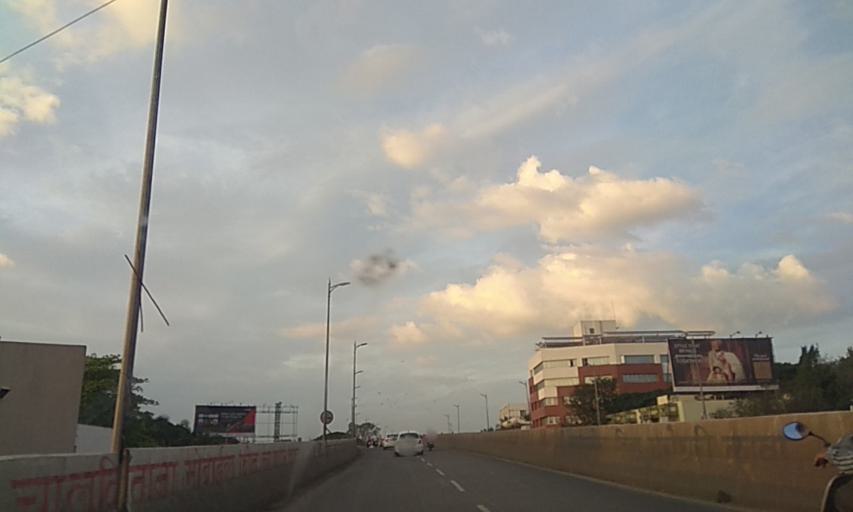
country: IN
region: Maharashtra
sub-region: Pune Division
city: Pune
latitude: 18.4954
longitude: 73.8577
